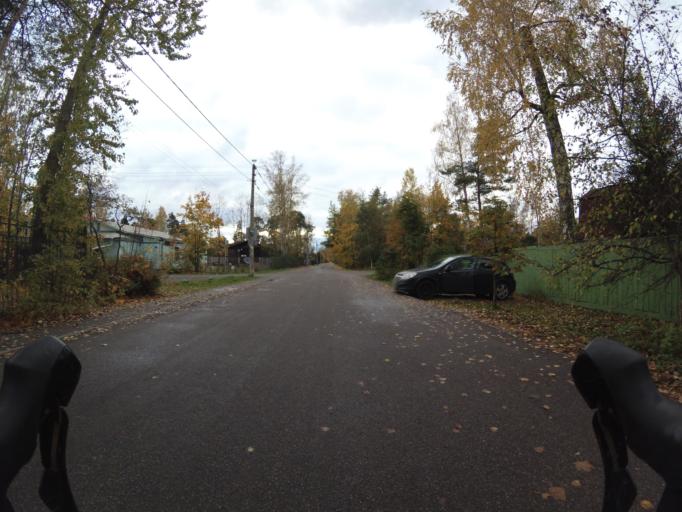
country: RU
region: St.-Petersburg
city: Lakhtinskiy
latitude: 59.9986
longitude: 30.1475
